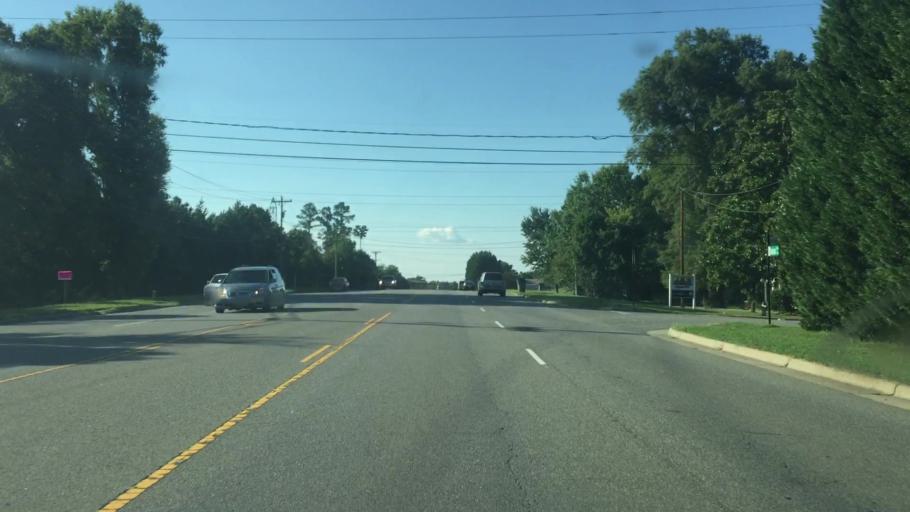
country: US
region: North Carolina
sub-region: Cabarrus County
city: Kannapolis
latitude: 35.4285
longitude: -80.6792
